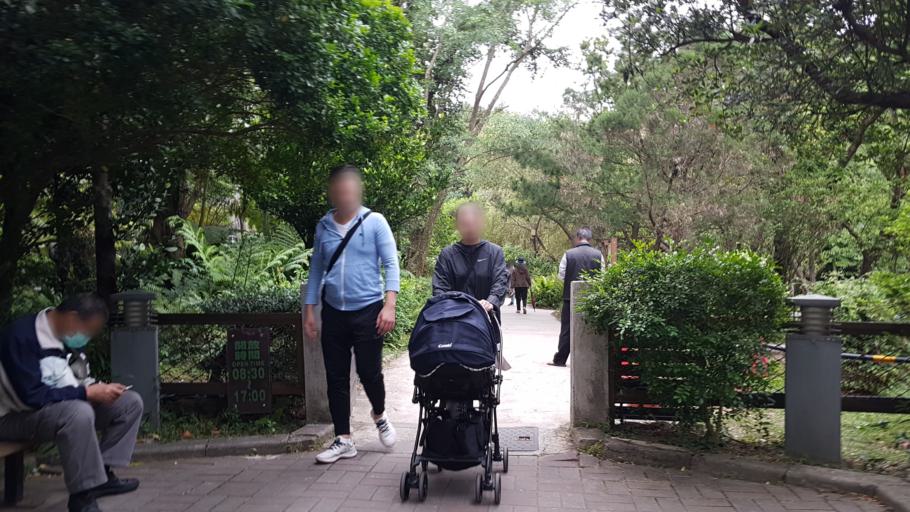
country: TW
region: Taipei
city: Taipei
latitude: 25.0327
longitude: 121.5088
